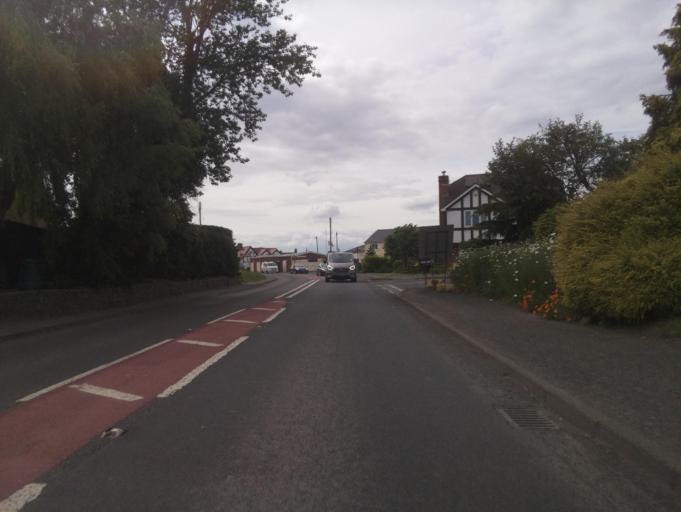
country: GB
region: England
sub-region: Worcestershire
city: Leigh
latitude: 52.1553
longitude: -2.3208
